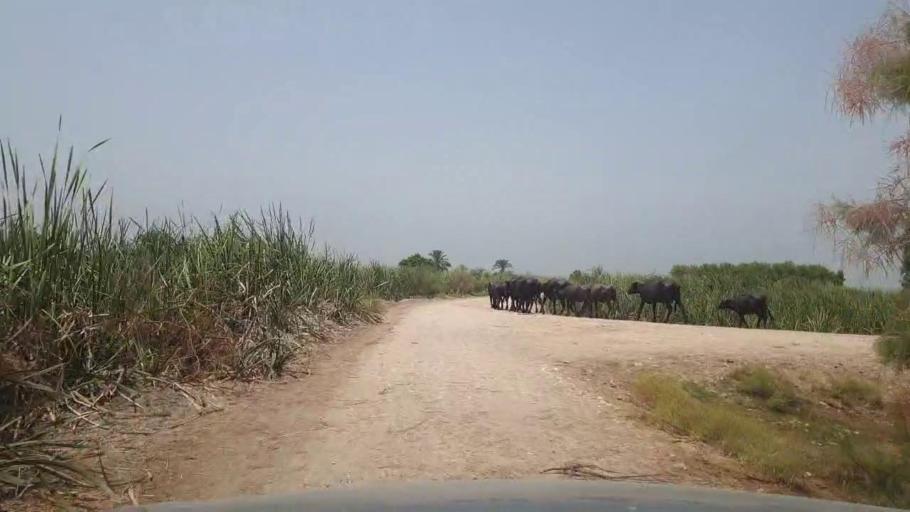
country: PK
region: Sindh
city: Garhi Yasin
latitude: 27.9545
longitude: 68.4351
